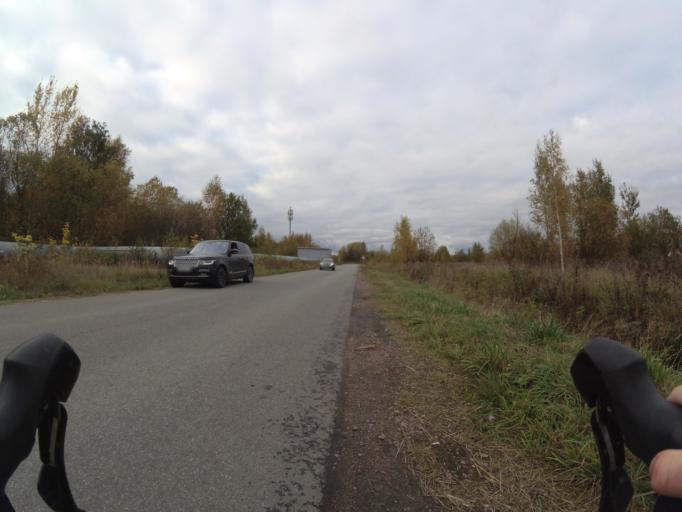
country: RU
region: St.-Petersburg
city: Lakhtinskiy
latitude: 60.0003
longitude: 30.1562
